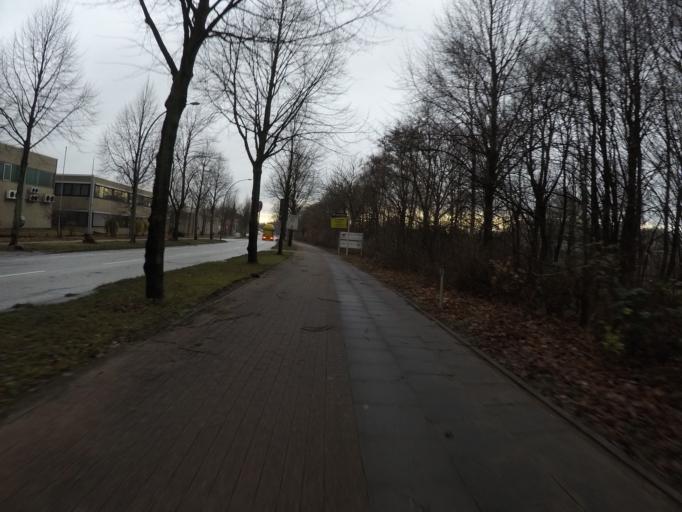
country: DE
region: Hamburg
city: Harburg
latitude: 53.4792
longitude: 9.9932
